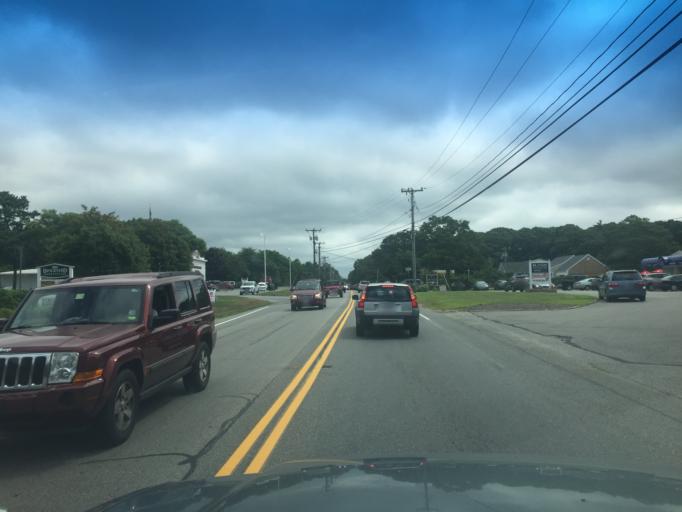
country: US
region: Massachusetts
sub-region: Barnstable County
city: Mashpee
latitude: 41.6157
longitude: -70.5201
